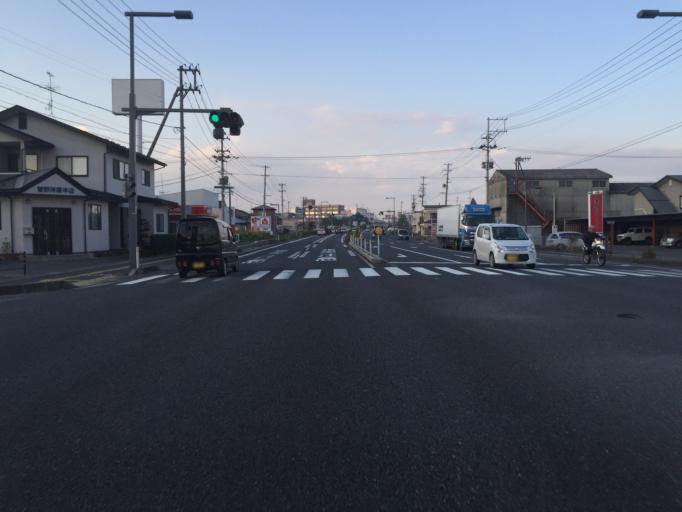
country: JP
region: Fukushima
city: Motomiya
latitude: 37.5154
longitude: 140.3952
